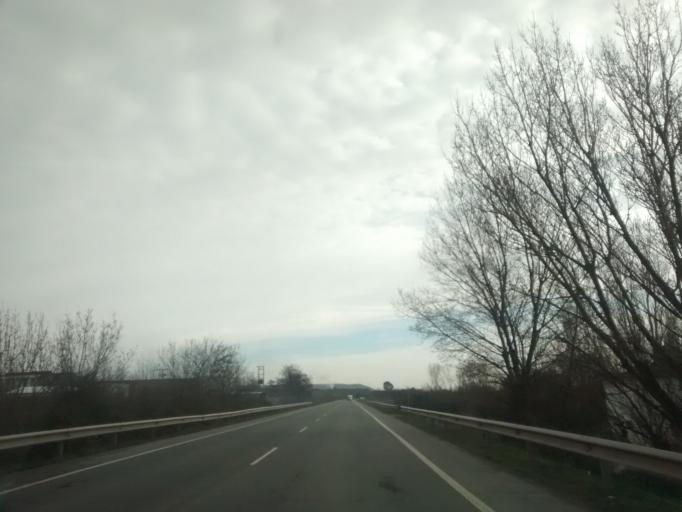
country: ES
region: Navarre
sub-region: Provincia de Navarra
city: Viana
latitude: 42.4749
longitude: -2.3851
